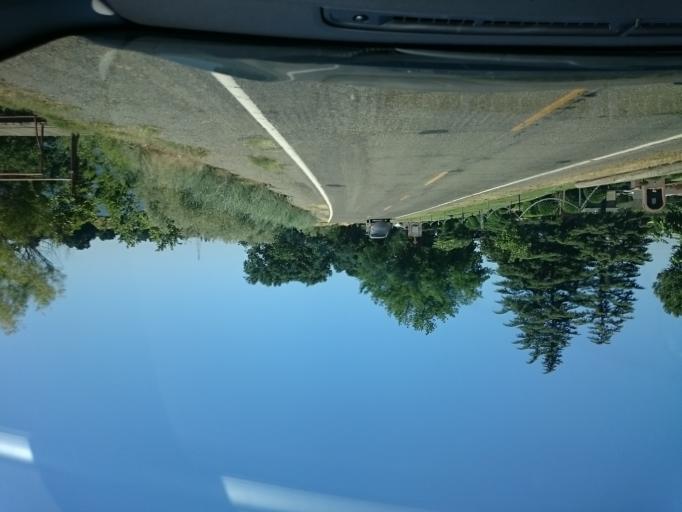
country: US
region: California
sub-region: Sacramento County
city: Parkway
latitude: 38.4598
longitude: -121.5044
